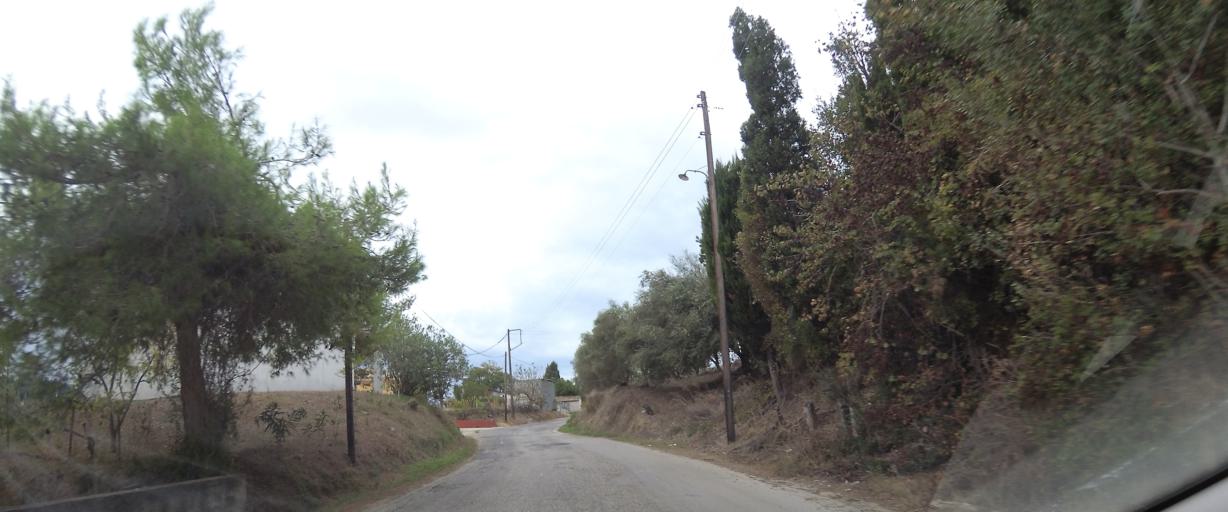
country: GR
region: Ionian Islands
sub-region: Nomos Kerkyras
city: Agios Georgis
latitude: 39.7477
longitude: 19.6831
